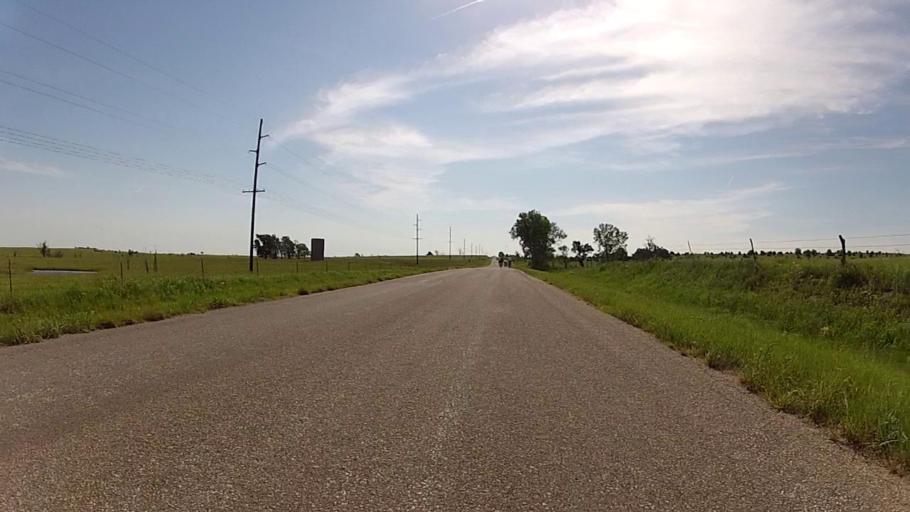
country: US
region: Kansas
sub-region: Cowley County
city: Winfield
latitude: 37.0710
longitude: -96.6553
